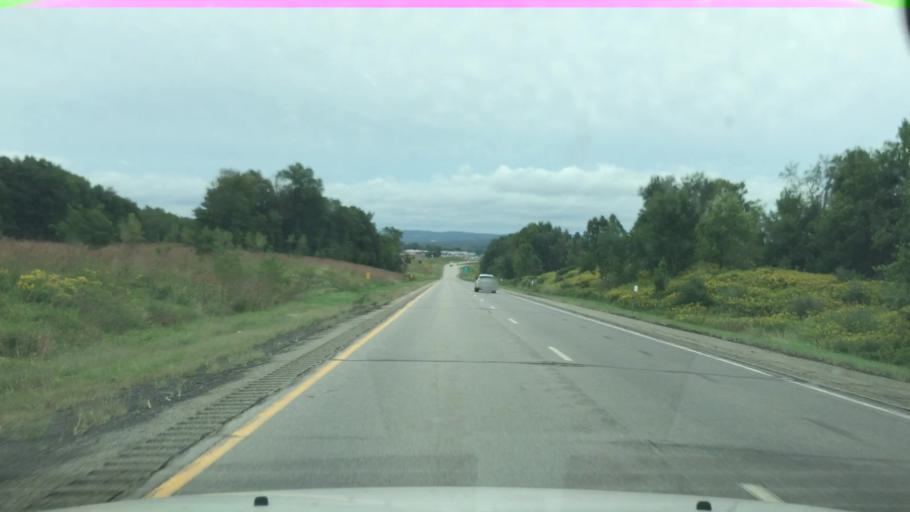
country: US
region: New York
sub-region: Erie County
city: Springville
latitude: 42.5201
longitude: -78.6975
